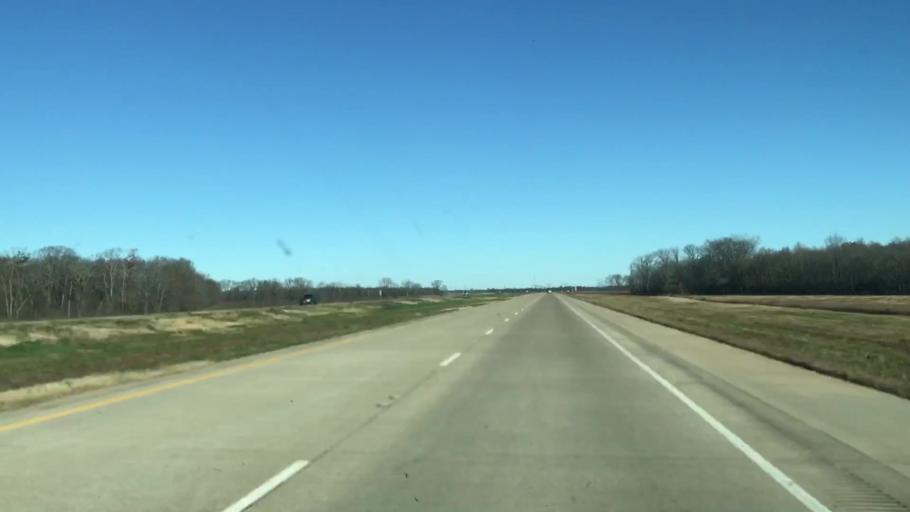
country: US
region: Louisiana
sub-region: Caddo Parish
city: Blanchard
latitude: 32.6410
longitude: -93.8384
